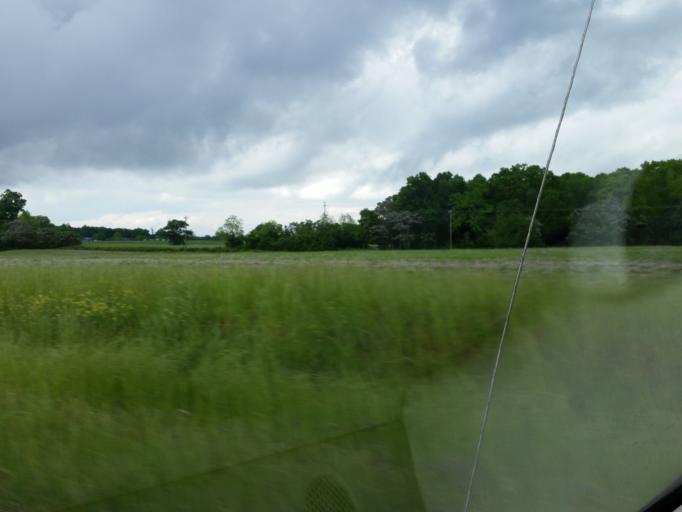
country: US
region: Georgia
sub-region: Dooly County
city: Unadilla
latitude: 32.3395
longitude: -83.7776
